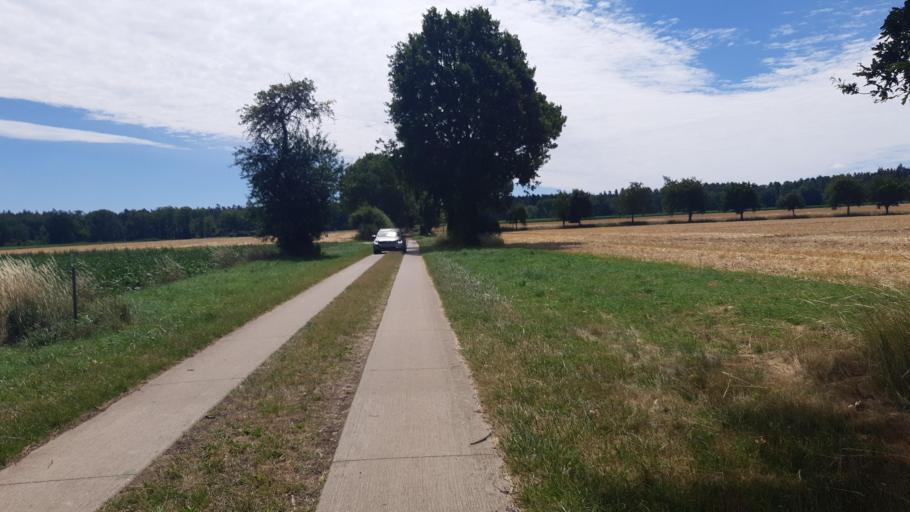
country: DE
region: Lower Saxony
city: Tosterglope
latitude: 53.2320
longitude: 10.7886
